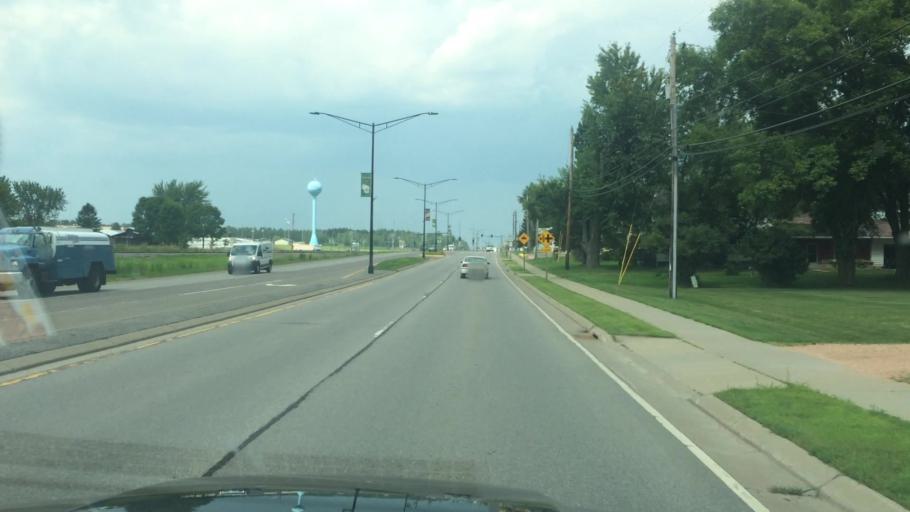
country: US
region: Wisconsin
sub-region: Clark County
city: Colby
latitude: 44.9141
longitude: -90.3154
